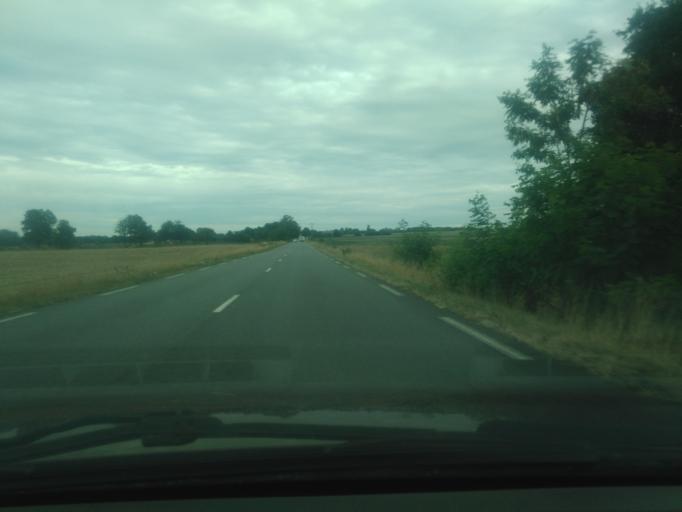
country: FR
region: Auvergne
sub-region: Departement de l'Allier
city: Ainay-le-Chateau
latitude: 46.7406
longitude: 2.7104
